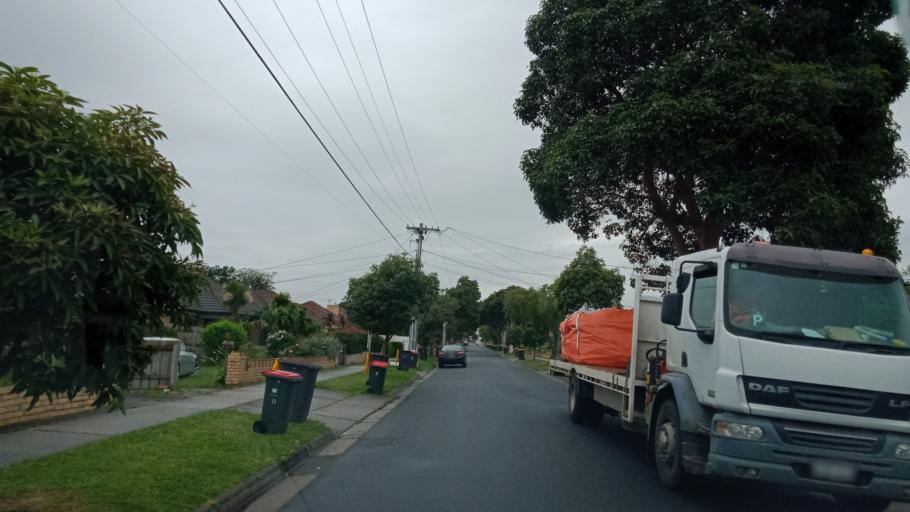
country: AU
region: Victoria
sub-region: Greater Dandenong
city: Springvale
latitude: -37.9316
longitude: 145.1615
